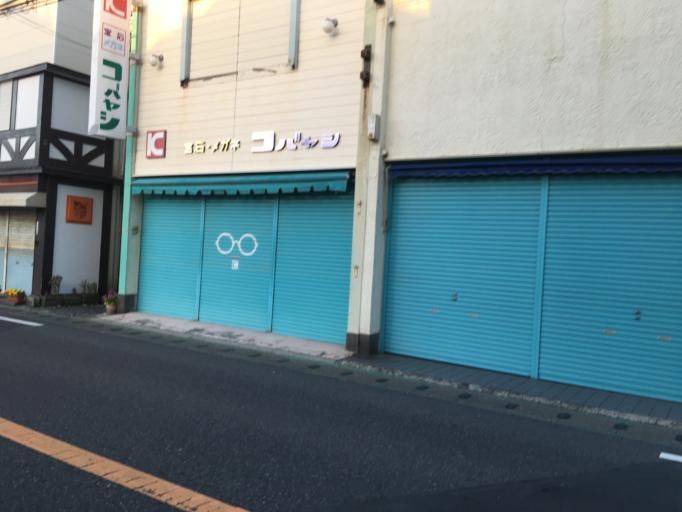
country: JP
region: Chiba
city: Tateyama
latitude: 34.9945
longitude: 139.8633
